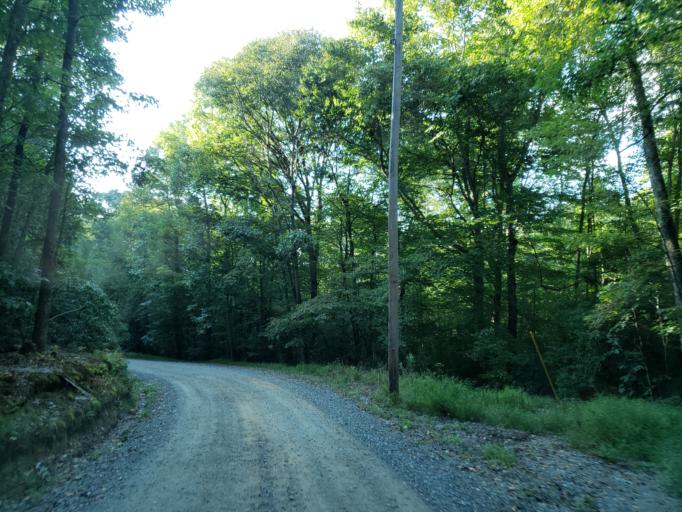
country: US
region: Georgia
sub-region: Fannin County
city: Blue Ridge
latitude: 34.6819
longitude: -84.2626
